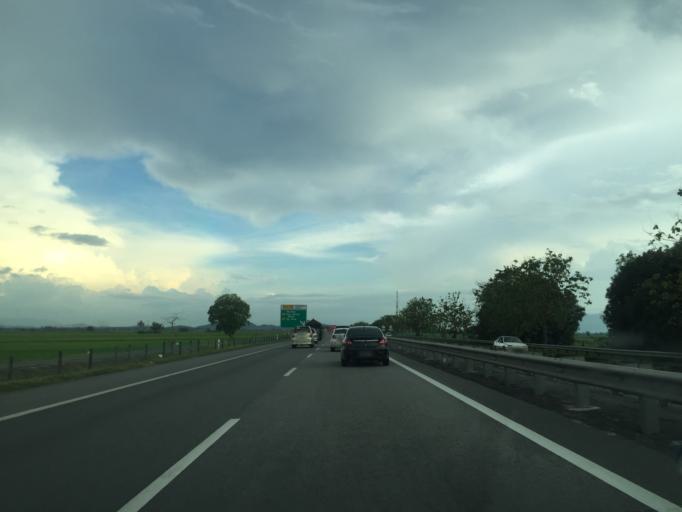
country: MY
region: Kedah
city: Alor Setar
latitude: 5.9985
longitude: 100.4263
